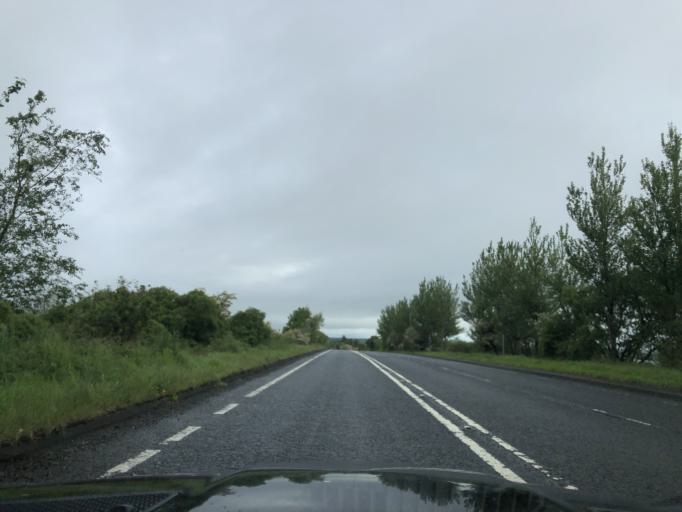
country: GB
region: Northern Ireland
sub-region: Ballymoney District
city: Ballymoney
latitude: 55.0601
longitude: -6.4682
